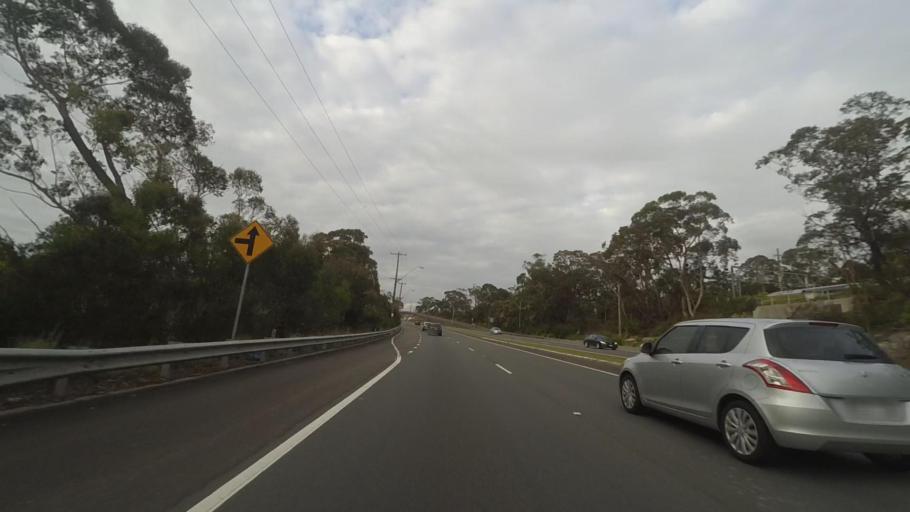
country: AU
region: New South Wales
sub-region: Wollongong
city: Helensburgh
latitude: -34.1382
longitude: 150.9942
